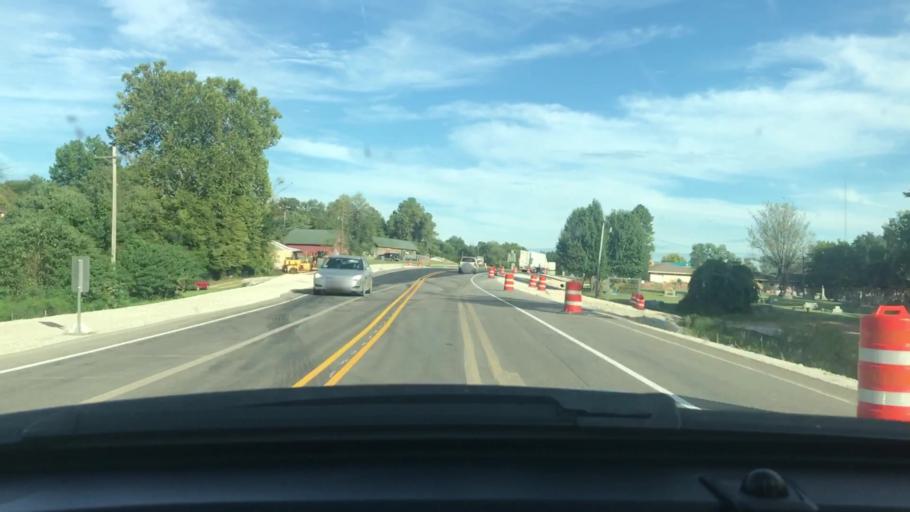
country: US
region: Arkansas
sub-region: Sharp County
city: Cherokee Village
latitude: 36.3035
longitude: -91.4475
